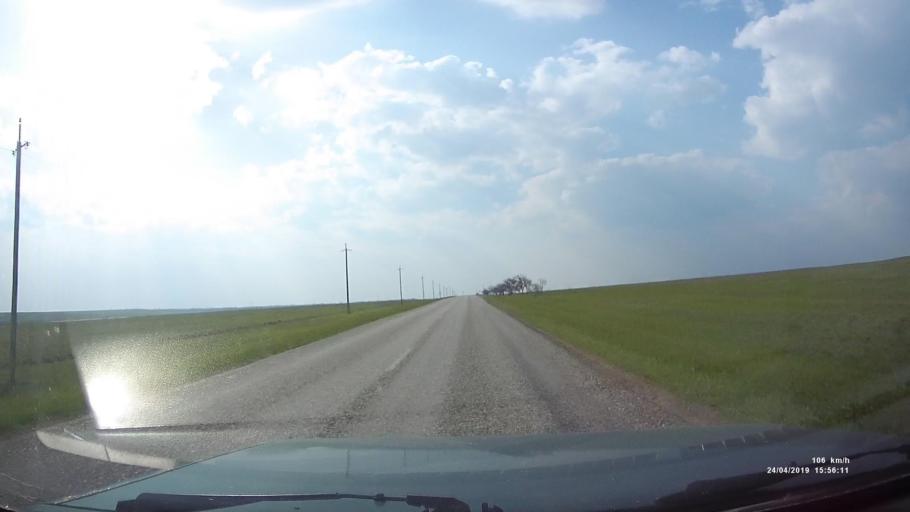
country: RU
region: Kalmykiya
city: Yashalta
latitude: 46.5958
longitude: 42.5340
